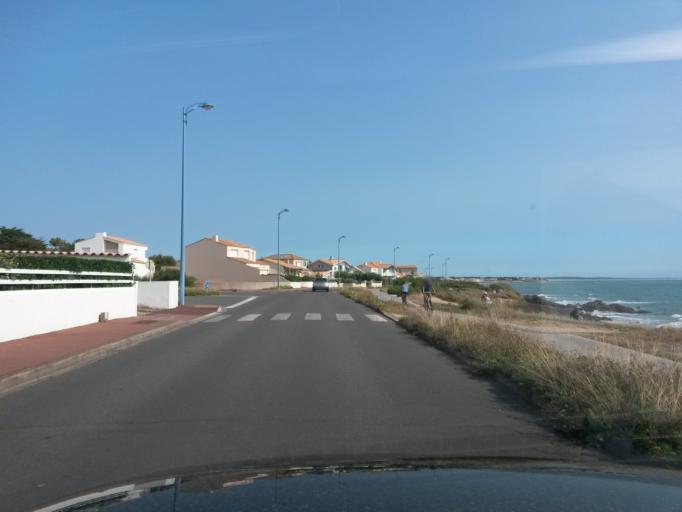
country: FR
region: Pays de la Loire
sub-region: Departement de la Vendee
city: Bretignolles-sur-Mer
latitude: 46.6345
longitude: -1.8885
